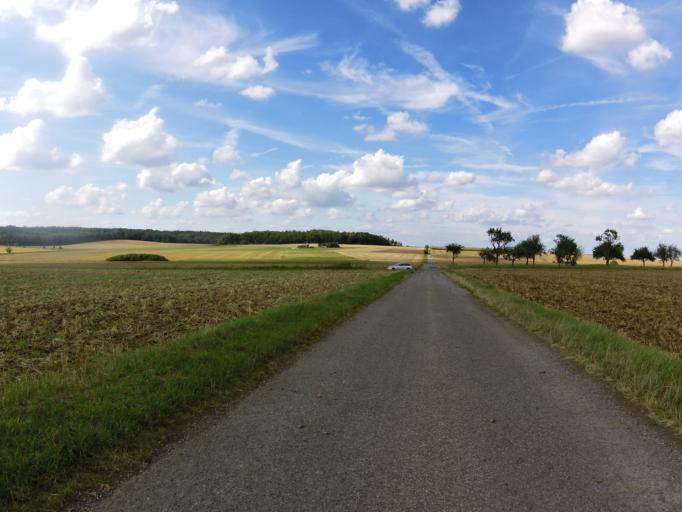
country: DE
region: Bavaria
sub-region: Regierungsbezirk Unterfranken
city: Geroldshausen
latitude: 49.7007
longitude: 9.8958
